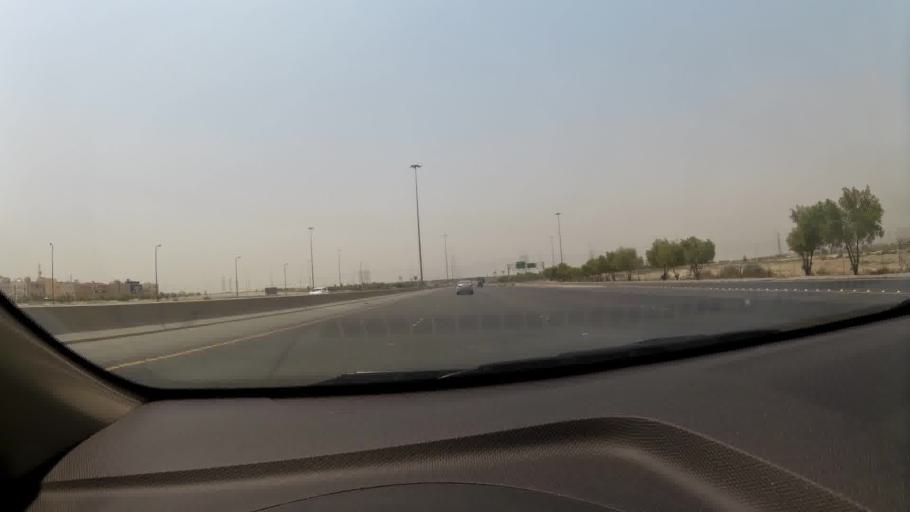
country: KW
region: Muhafazat al Jahra'
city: Al Jahra'
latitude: 29.3116
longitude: 47.7919
